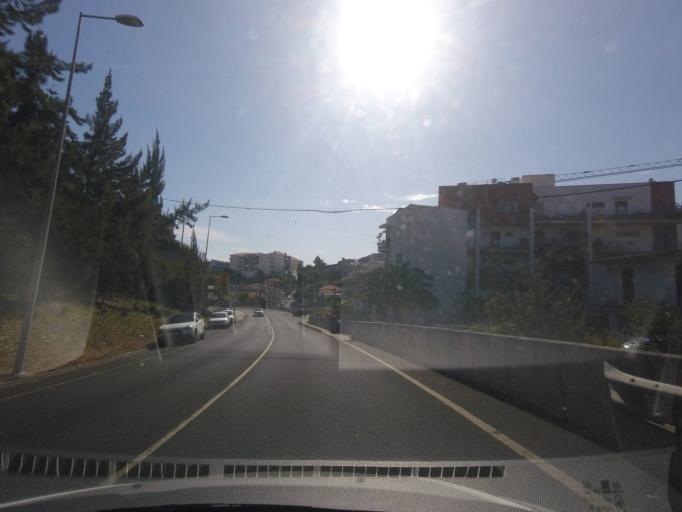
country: PT
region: Madeira
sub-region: Funchal
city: Funchal
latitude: 32.6498
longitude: -16.9269
